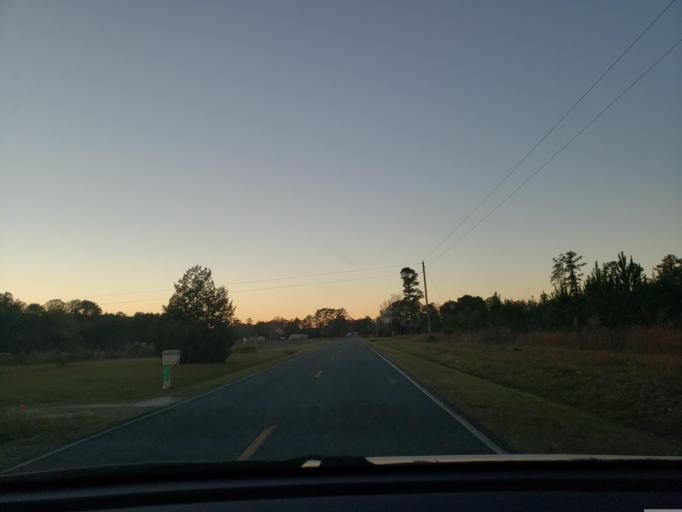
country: US
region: North Carolina
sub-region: Onslow County
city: Richlands
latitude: 34.7393
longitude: -77.6302
